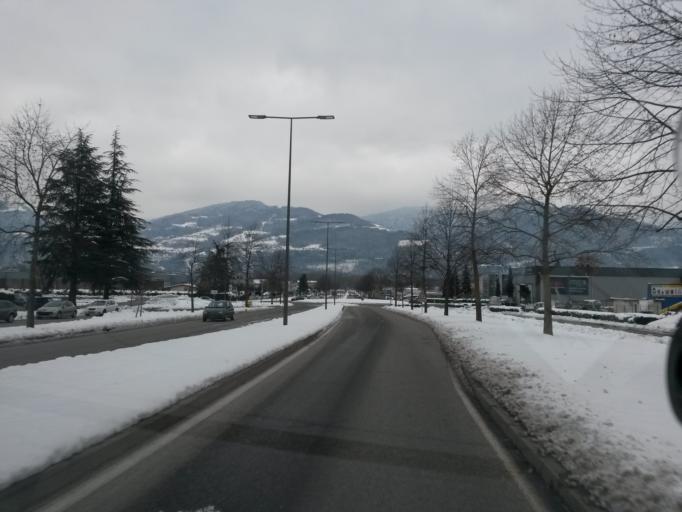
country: FR
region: Rhone-Alpes
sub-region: Departement de l'Isere
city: Crolles
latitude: 45.2739
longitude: 5.8835
